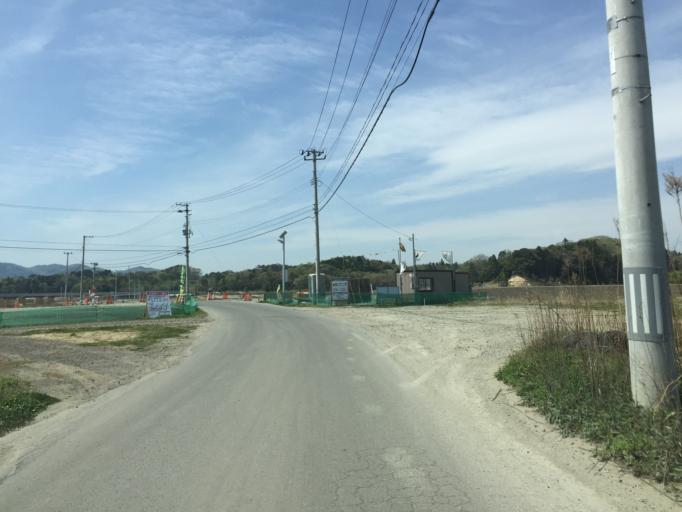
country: JP
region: Miyagi
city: Watari
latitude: 37.9018
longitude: 140.9228
